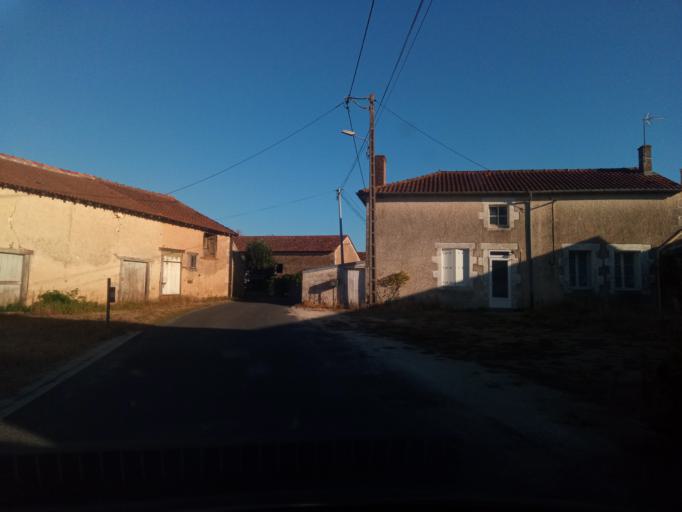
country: FR
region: Poitou-Charentes
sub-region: Departement de la Vienne
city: Montmorillon
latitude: 46.4074
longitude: 0.8699
